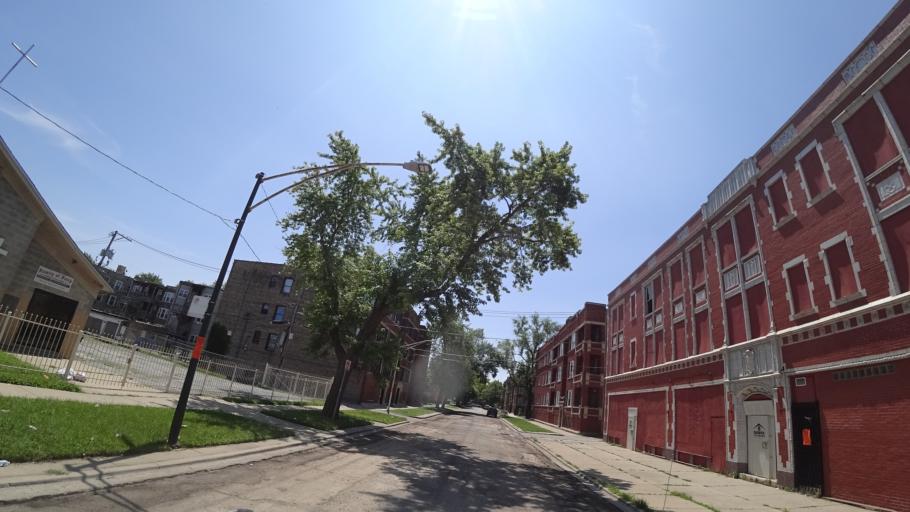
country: US
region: Illinois
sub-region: Cook County
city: Chicago
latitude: 41.7732
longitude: -87.5888
